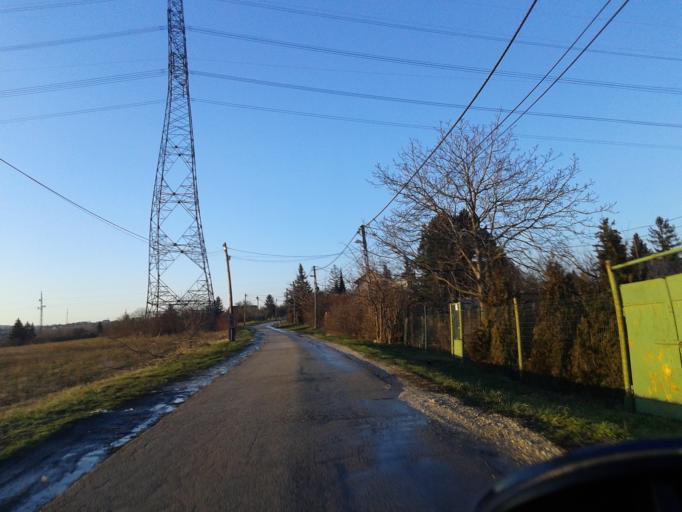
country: HU
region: Pest
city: Diosd
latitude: 47.4078
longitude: 18.9690
